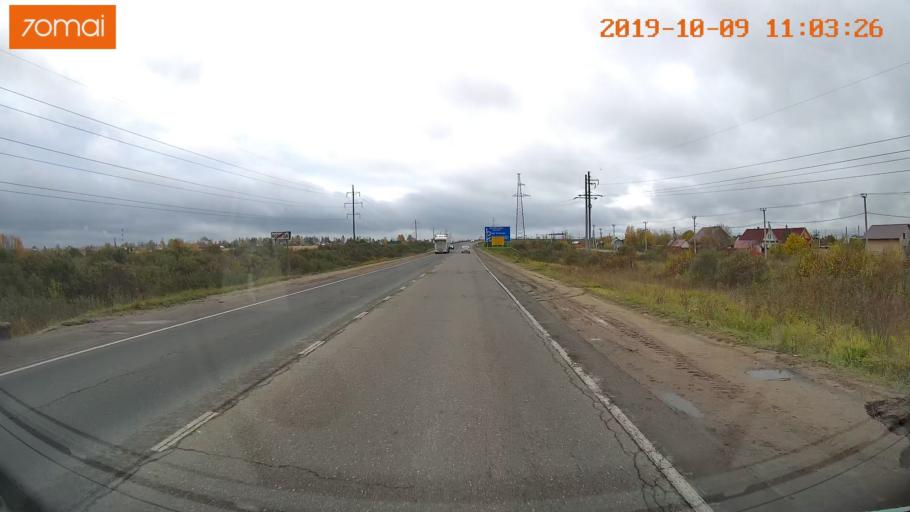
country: RU
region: Vologda
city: Vologda
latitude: 59.2219
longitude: 39.7746
